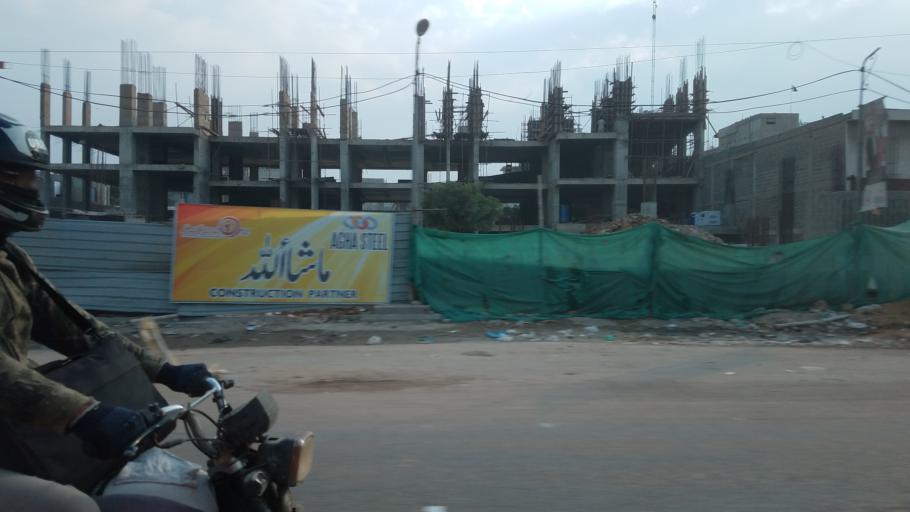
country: PK
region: Sindh
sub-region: Karachi District
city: Karachi
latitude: 24.9343
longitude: 67.0857
